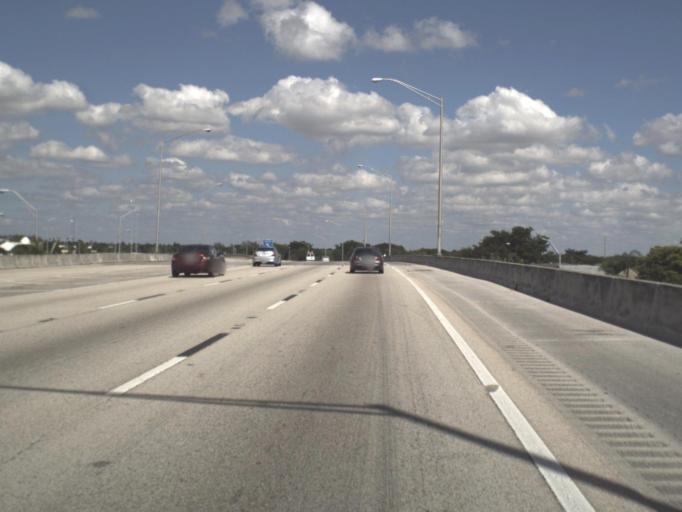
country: US
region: Florida
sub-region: Miami-Dade County
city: Three Lakes
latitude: 25.6563
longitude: -80.3856
